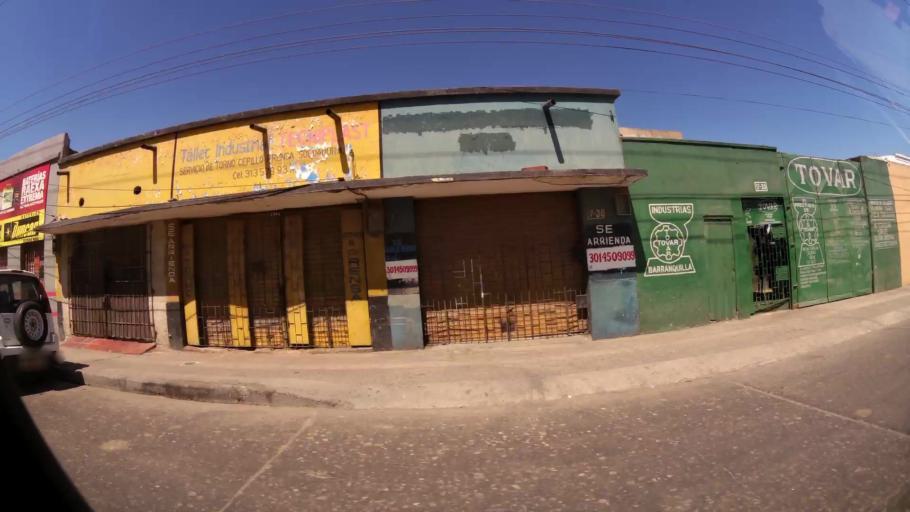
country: CO
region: Atlantico
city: Barranquilla
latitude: 10.9756
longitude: -74.7758
